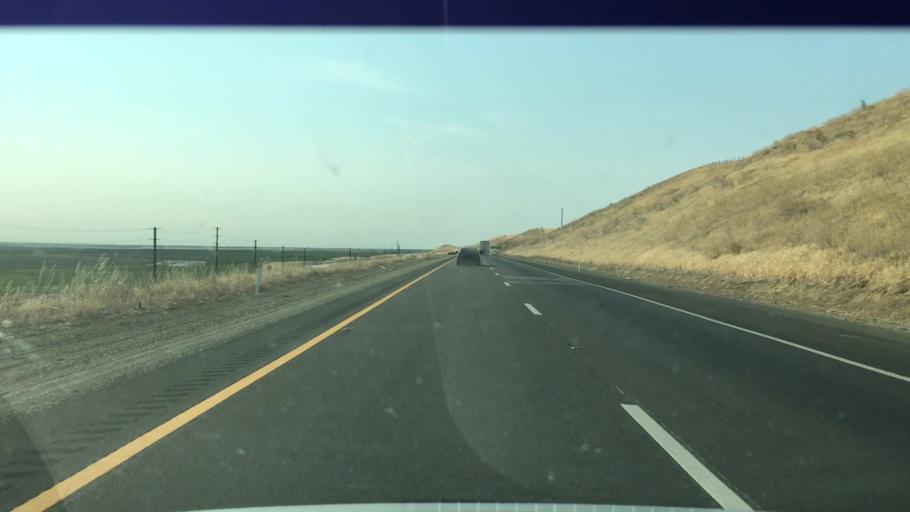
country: US
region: California
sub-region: Stanislaus County
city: Patterson
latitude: 37.4553
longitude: -121.1744
